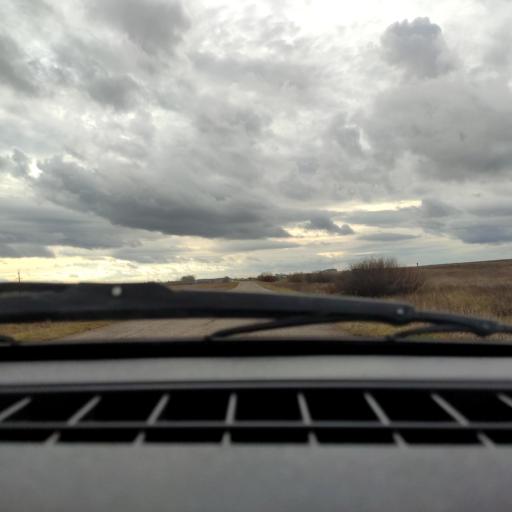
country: RU
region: Bashkortostan
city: Asanovo
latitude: 54.9201
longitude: 55.5096
